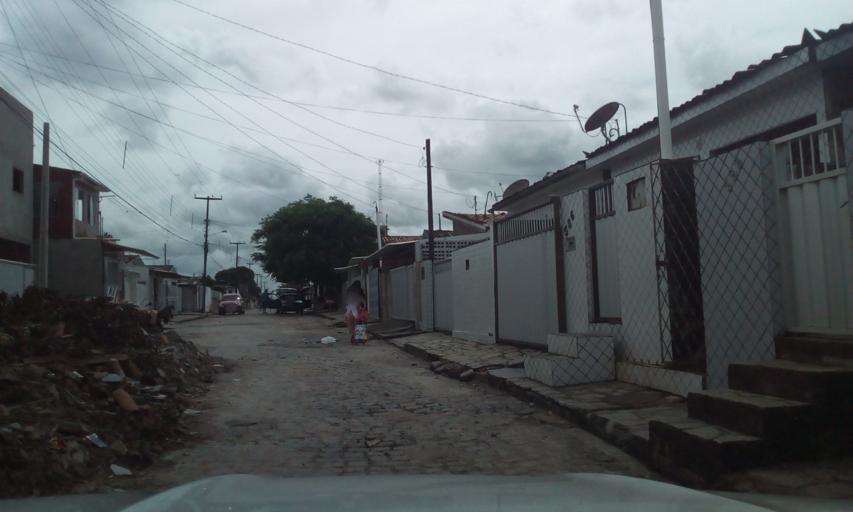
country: BR
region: Paraiba
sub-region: Bayeux
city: Bayeux
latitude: -7.1246
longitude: -34.9068
